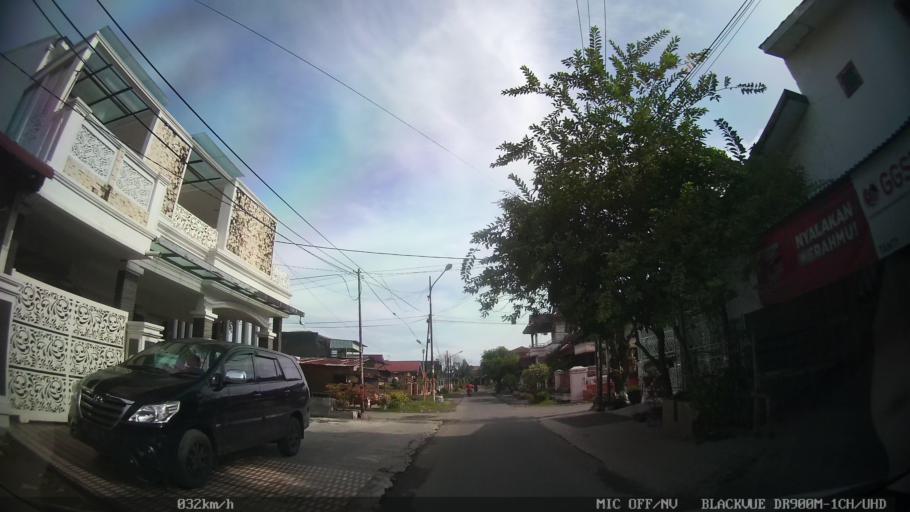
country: ID
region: North Sumatra
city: Sunggal
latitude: 3.6085
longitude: 98.6289
